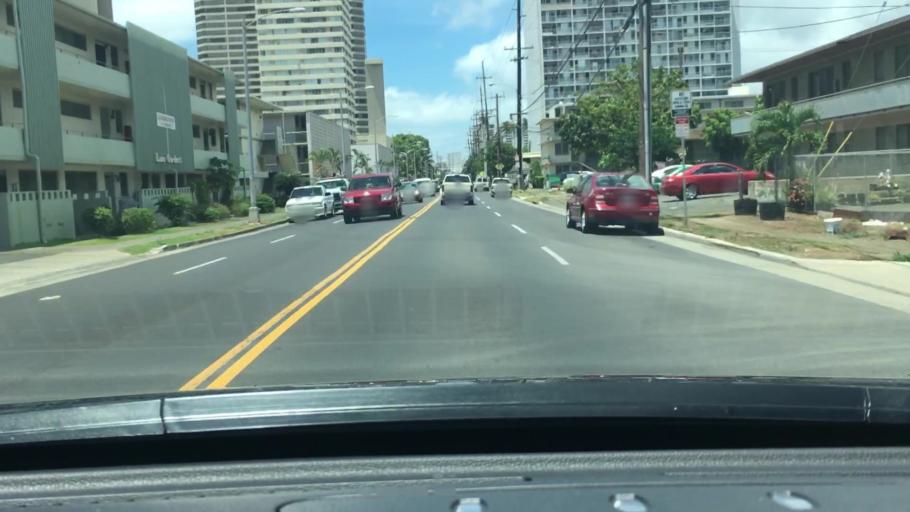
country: US
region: Hawaii
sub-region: Honolulu County
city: Honolulu
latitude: 21.2853
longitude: -157.8211
